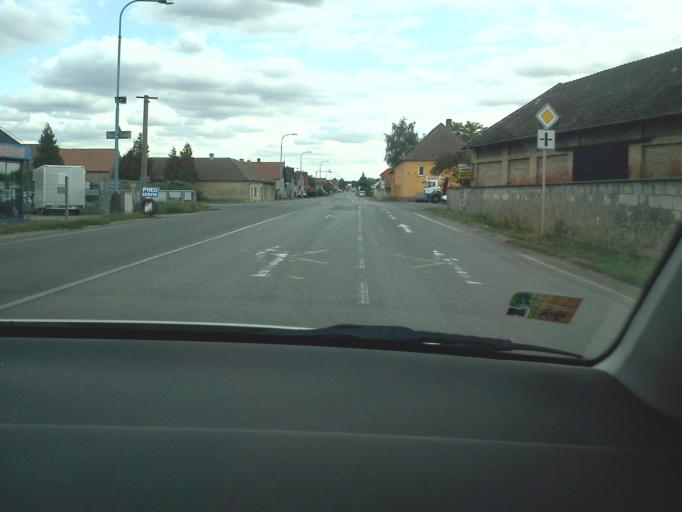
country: CZ
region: Central Bohemia
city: Prerov nad Labem
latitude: 50.1452
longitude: 14.8447
